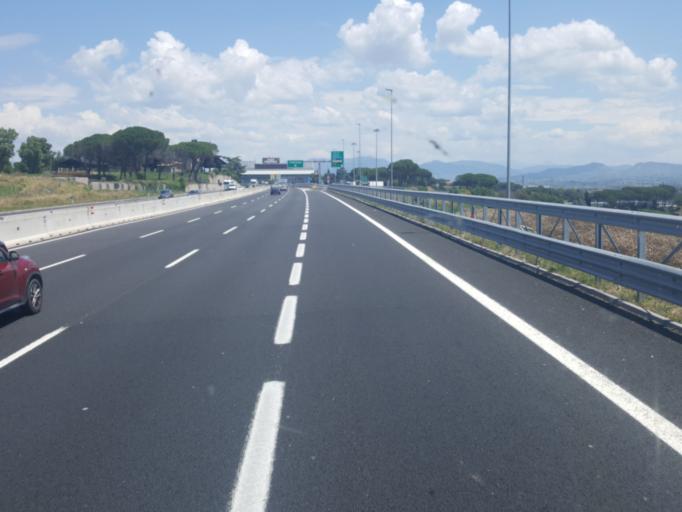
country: IT
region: Latium
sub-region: Citta metropolitana di Roma Capitale
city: Bivio di Capanelle
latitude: 42.1302
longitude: 12.6000
